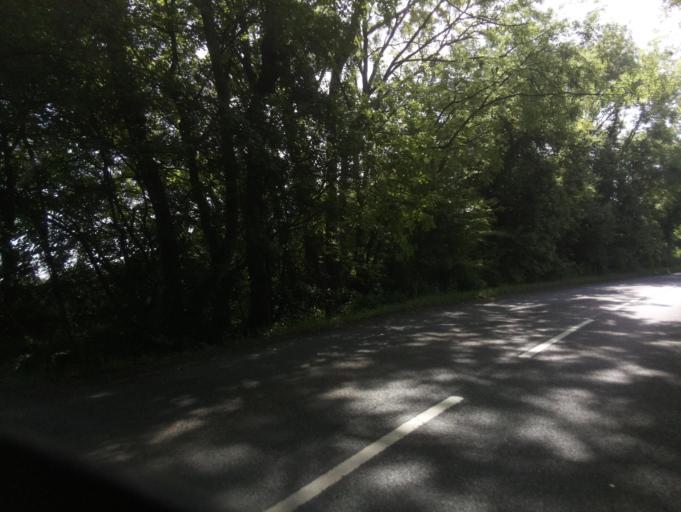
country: GB
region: England
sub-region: Lincolnshire
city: Skellingthorpe
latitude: 53.1577
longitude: -0.6333
